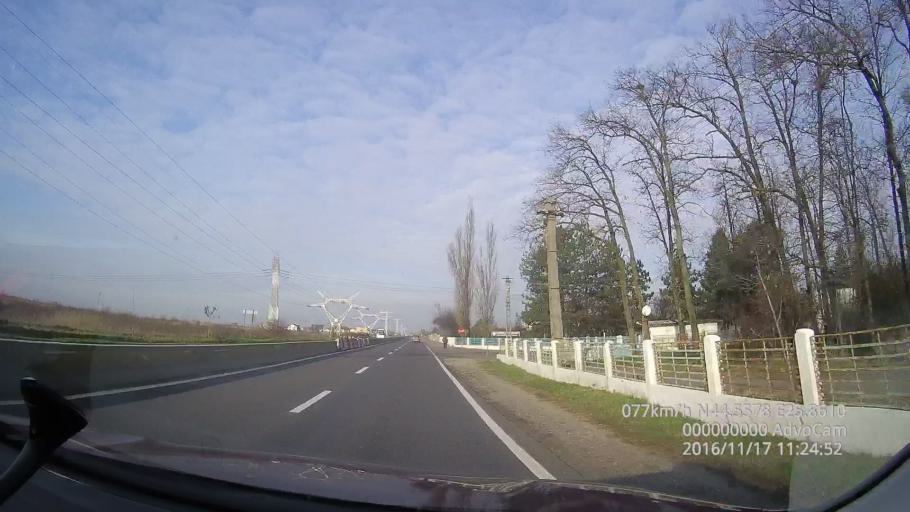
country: RO
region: Dambovita
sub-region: Comuna Tartasesti
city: Gulia
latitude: 44.5580
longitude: 25.8606
